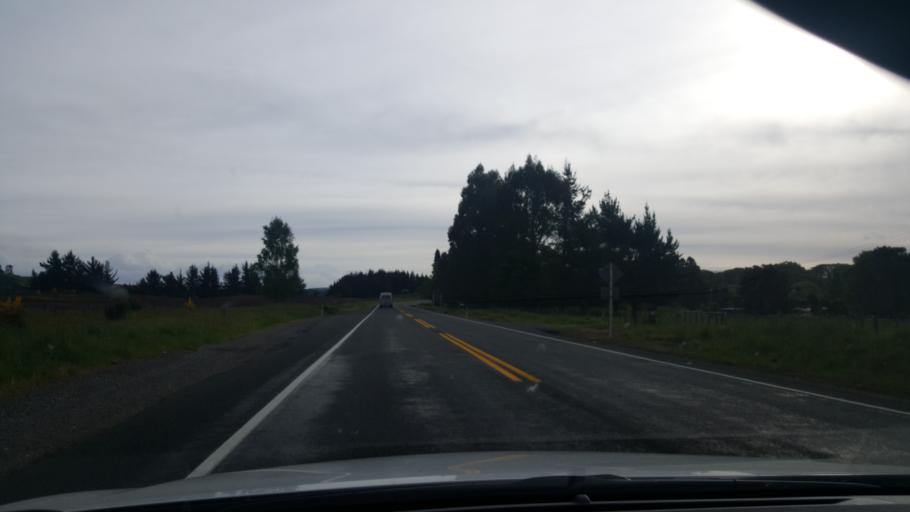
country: NZ
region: Waikato
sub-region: Taupo District
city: Taupo
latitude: -38.6121
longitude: 176.1191
